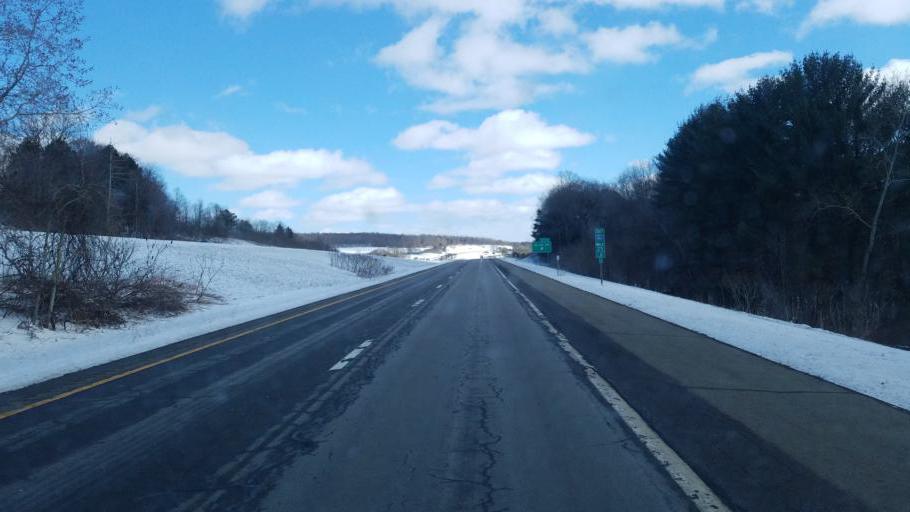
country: US
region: New York
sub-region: Chautauqua County
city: Celoron
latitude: 42.1264
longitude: -79.2831
